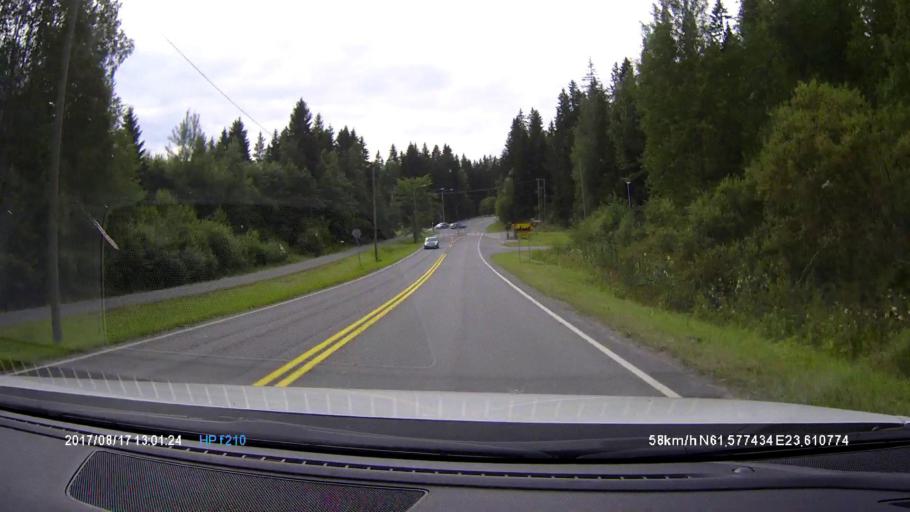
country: FI
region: Pirkanmaa
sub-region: Tampere
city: Yloejaervi
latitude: 61.5768
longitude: 23.6105
